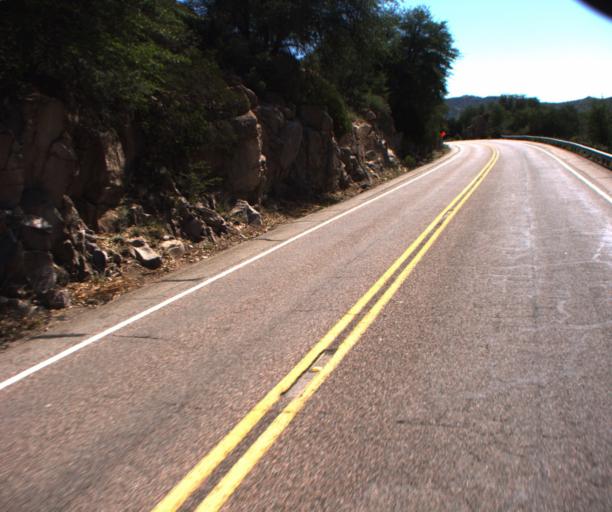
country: US
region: Arizona
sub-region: Pinal County
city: Superior
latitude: 33.3415
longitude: -111.0118
